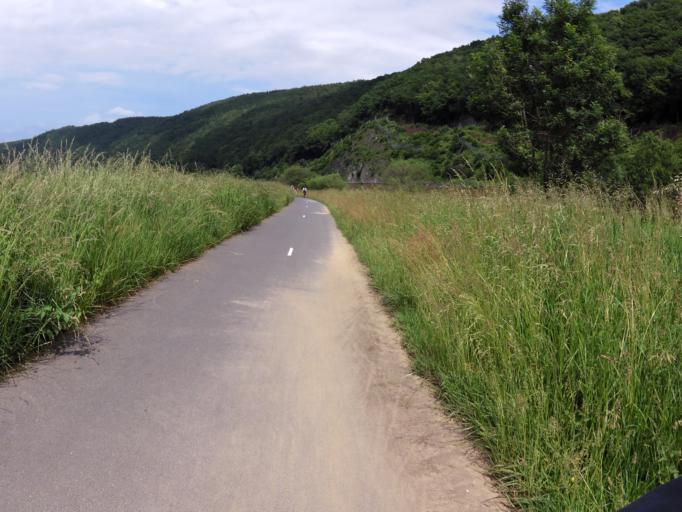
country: FR
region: Champagne-Ardenne
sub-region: Departement des Ardennes
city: Neufmanil
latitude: 49.8329
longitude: 4.7781
